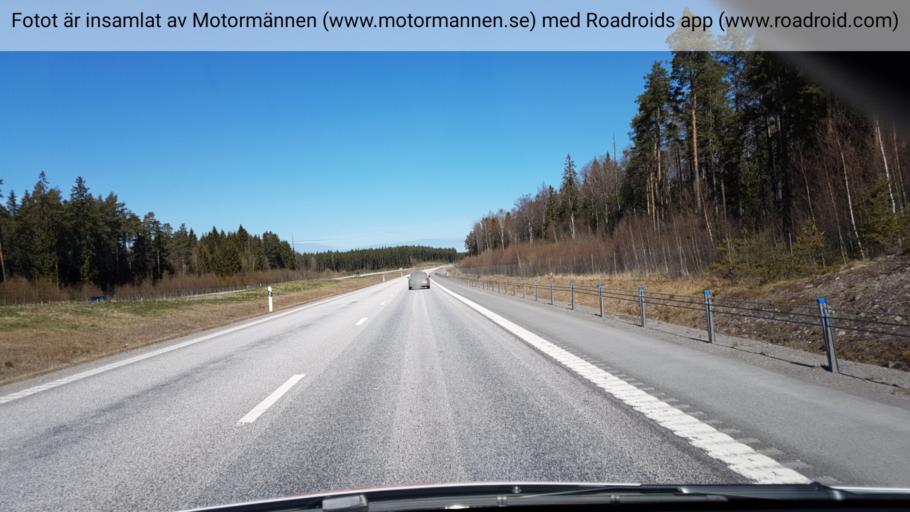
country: SE
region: Uppsala
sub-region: Tierps Kommun
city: Tierp
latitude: 60.2722
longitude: 17.5018
